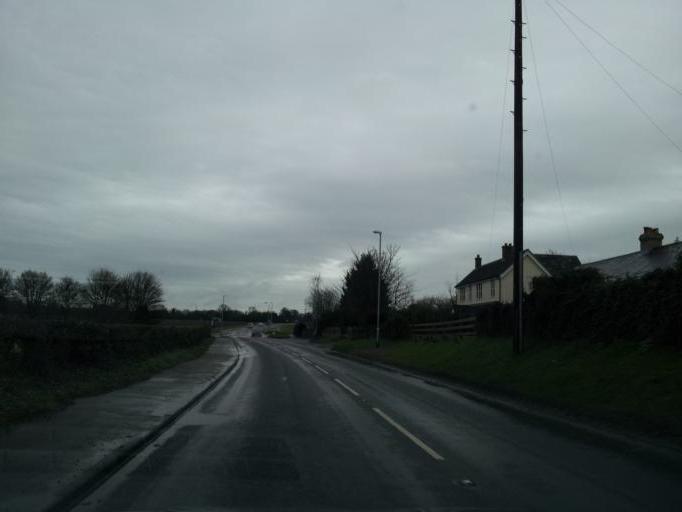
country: GB
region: England
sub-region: Cambridgeshire
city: Bottisham
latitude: 52.2411
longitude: 0.2812
